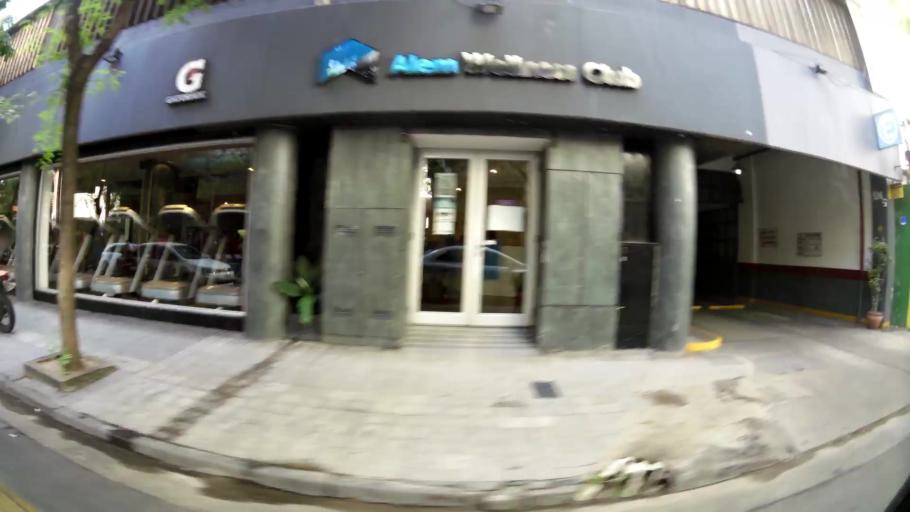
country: AR
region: Santa Fe
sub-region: Departamento de Rosario
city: Rosario
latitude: -32.9536
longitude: -60.6297
